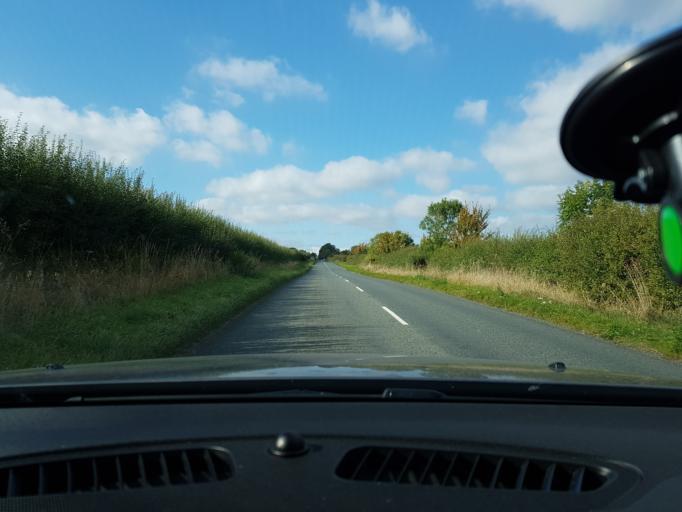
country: GB
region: England
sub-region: Wiltshire
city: Aldbourne
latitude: 51.4923
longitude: -1.6472
